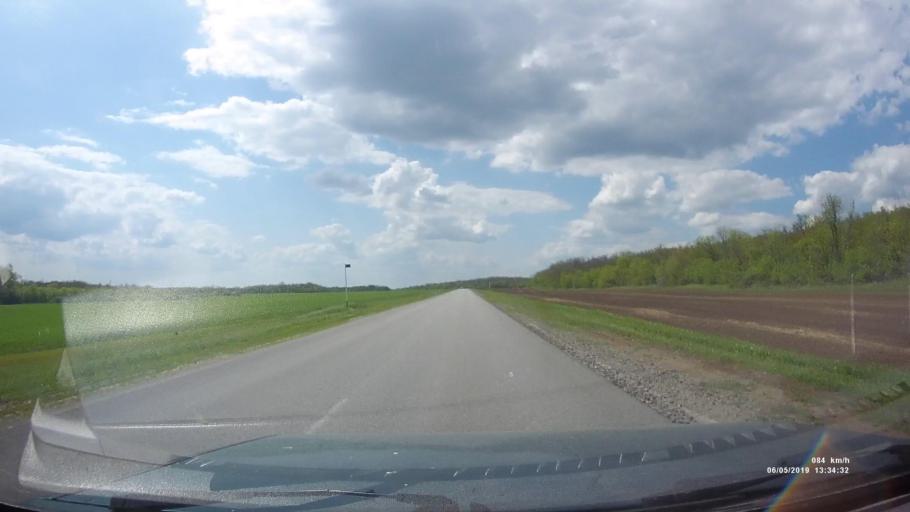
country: RU
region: Rostov
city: Ust'-Donetskiy
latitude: 47.6930
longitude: 40.7611
